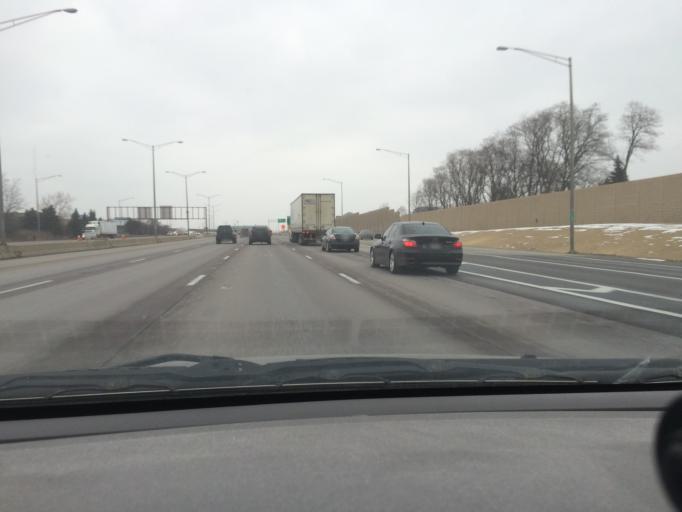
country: US
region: Illinois
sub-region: DuPage County
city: Itasca
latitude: 41.9765
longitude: -88.0237
